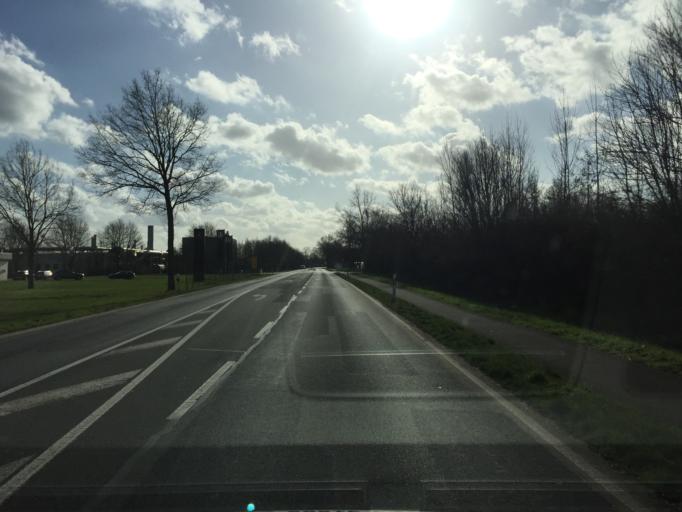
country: DE
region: Lower Saxony
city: Stolzenau
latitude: 52.5275
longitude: 9.0768
